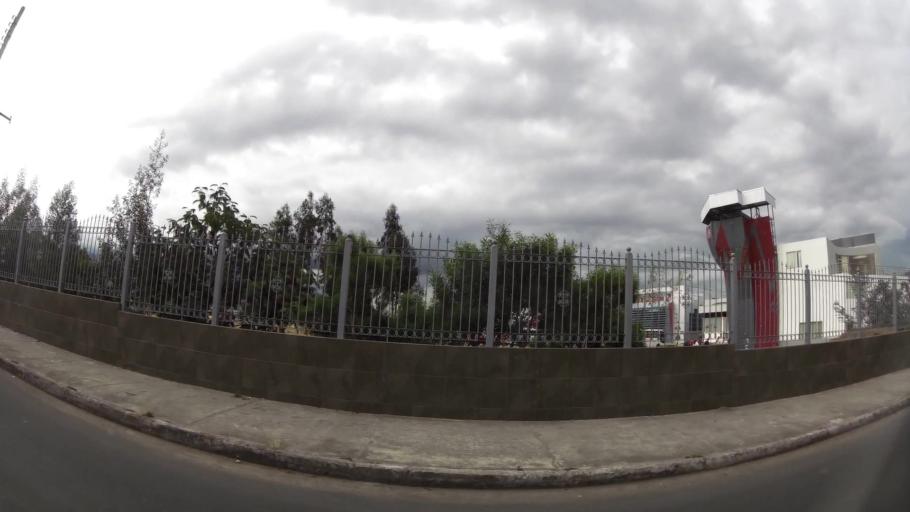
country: EC
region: Tungurahua
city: Ambato
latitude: -1.2706
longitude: -78.6251
